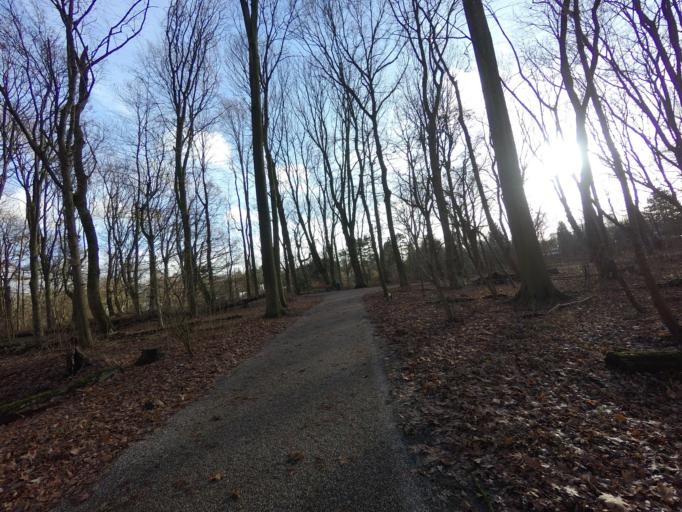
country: NL
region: South Holland
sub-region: Gemeente Rotterdam
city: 's-Gravenland
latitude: 51.9277
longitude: 4.5307
